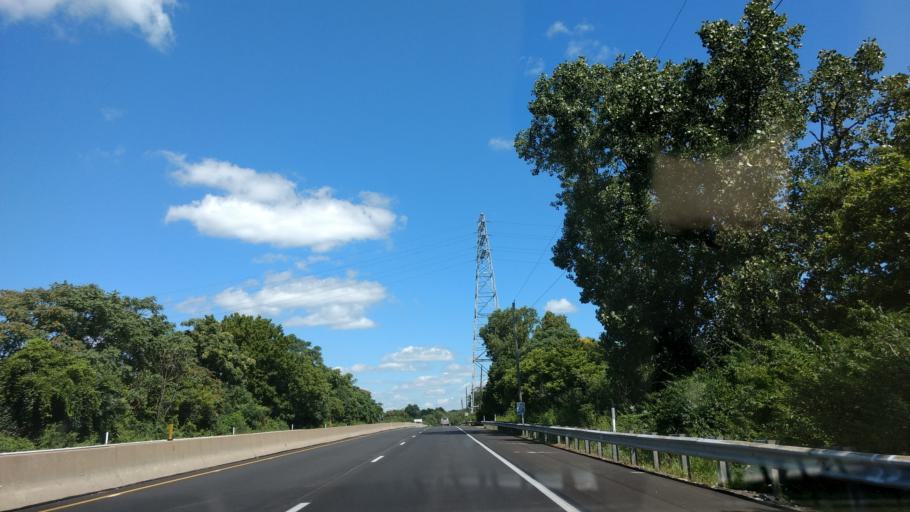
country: US
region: Pennsylvania
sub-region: Beaver County
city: Economy
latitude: 40.6115
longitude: -80.2316
